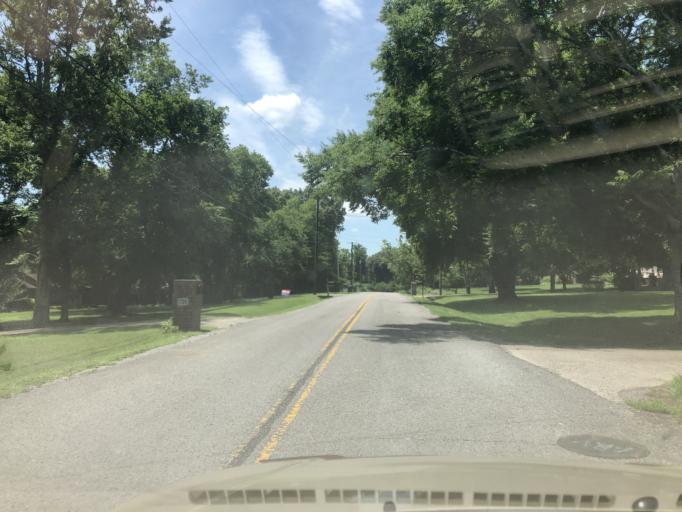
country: US
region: Tennessee
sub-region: Davidson County
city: Lakewood
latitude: 36.2502
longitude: -86.6920
